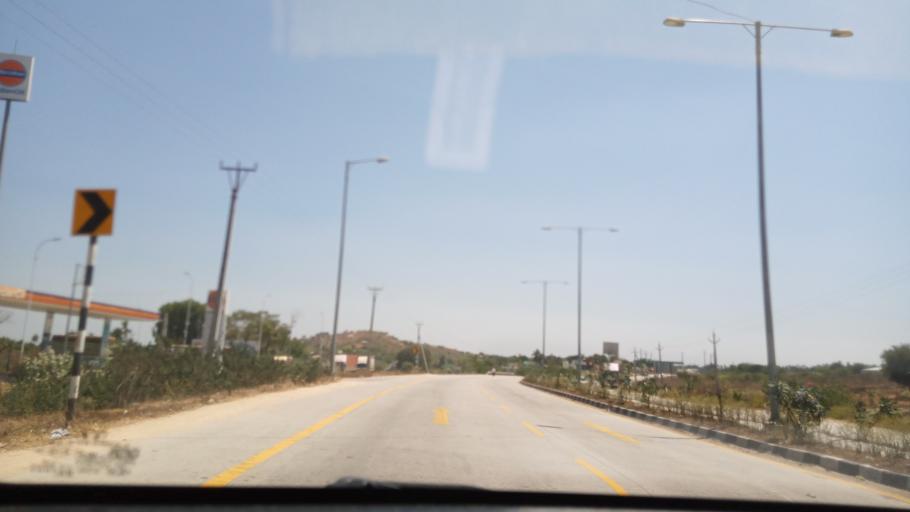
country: IN
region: Andhra Pradesh
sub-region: Chittoor
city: Chittoor
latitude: 13.2048
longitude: 78.9422
